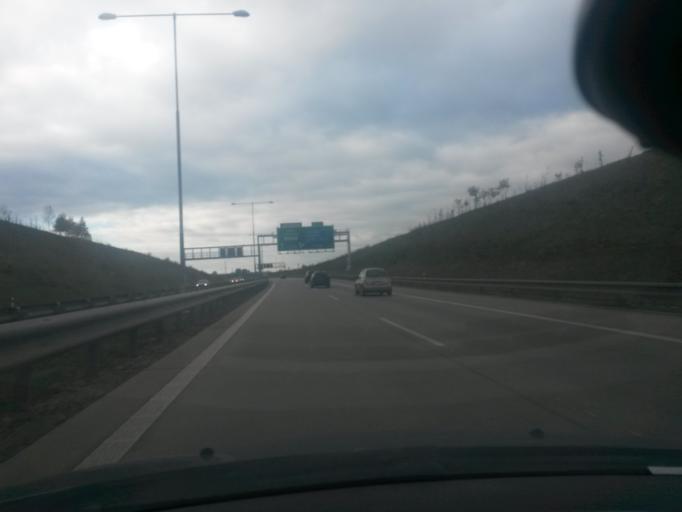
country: CZ
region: Central Bohemia
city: Jesenice
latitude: 49.9627
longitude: 14.5345
